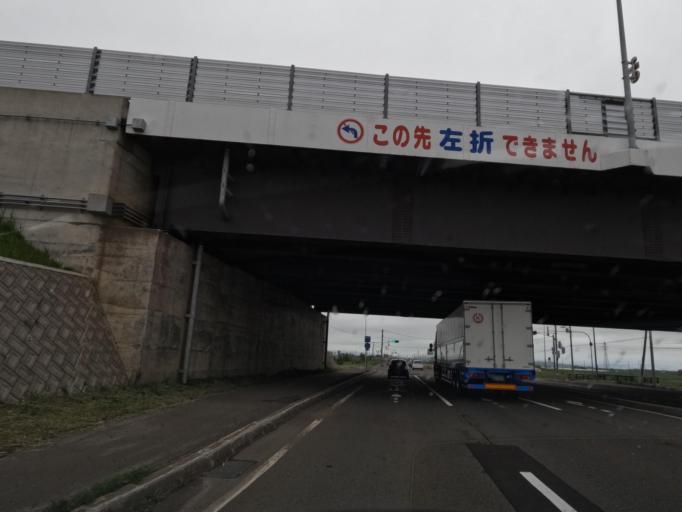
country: JP
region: Hokkaido
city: Tobetsu
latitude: 43.1837
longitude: 141.5234
